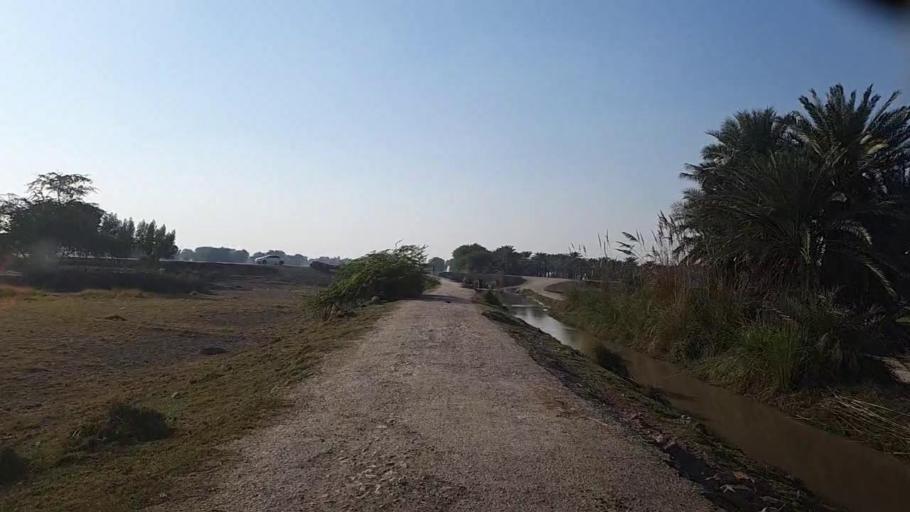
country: PK
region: Sindh
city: Ranipur
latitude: 27.2539
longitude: 68.5329
